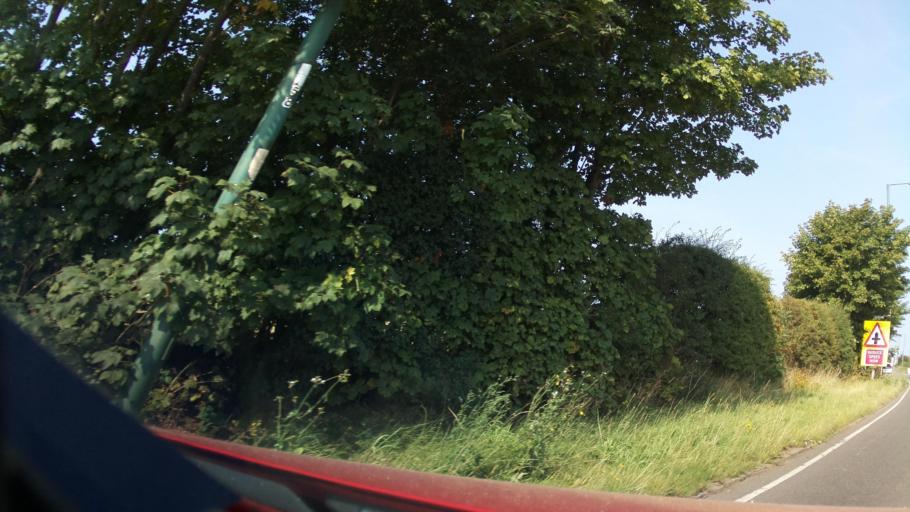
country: GB
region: England
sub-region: Walsall
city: Aldridge
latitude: 52.6212
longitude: -1.8925
